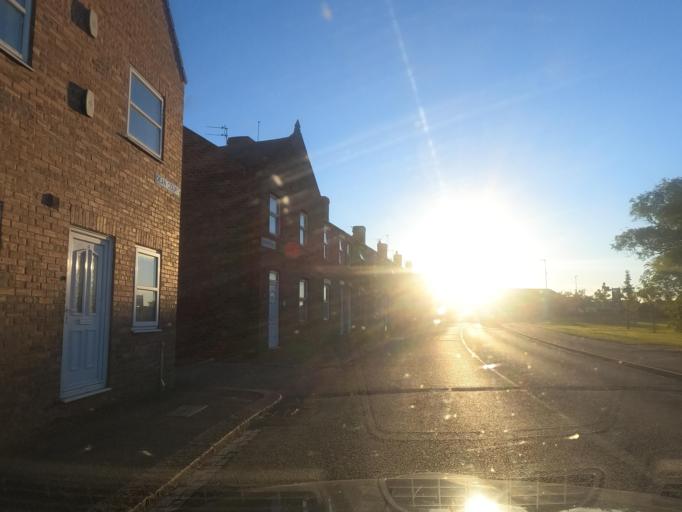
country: GB
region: England
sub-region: Northumberland
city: Blyth
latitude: 55.1276
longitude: -1.5196
